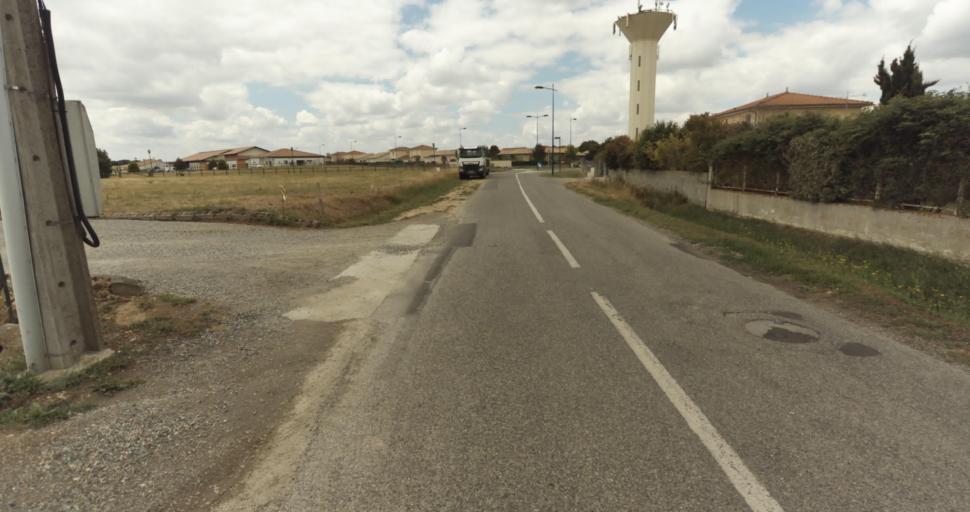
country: FR
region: Midi-Pyrenees
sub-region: Departement de la Haute-Garonne
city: Fontenilles
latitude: 43.5494
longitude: 1.1936
